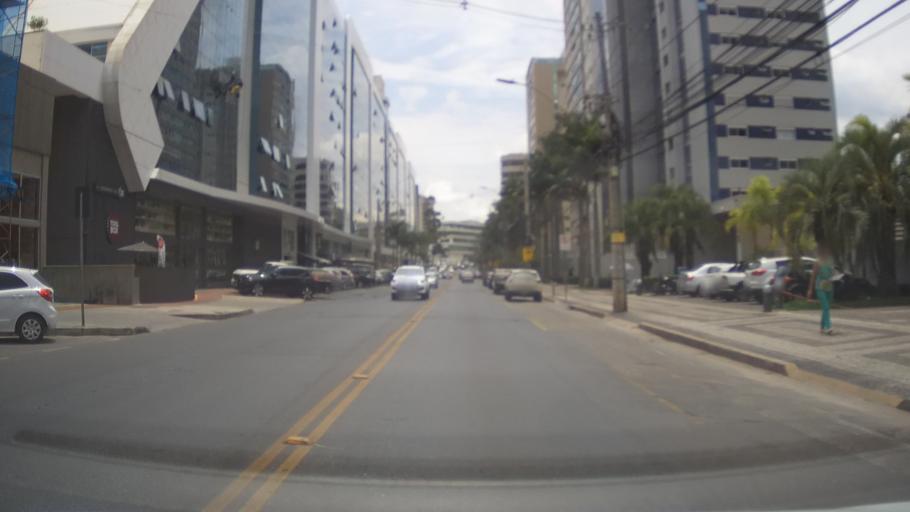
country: BR
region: Minas Gerais
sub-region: Belo Horizonte
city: Belo Horizonte
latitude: -19.9775
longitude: -43.9413
